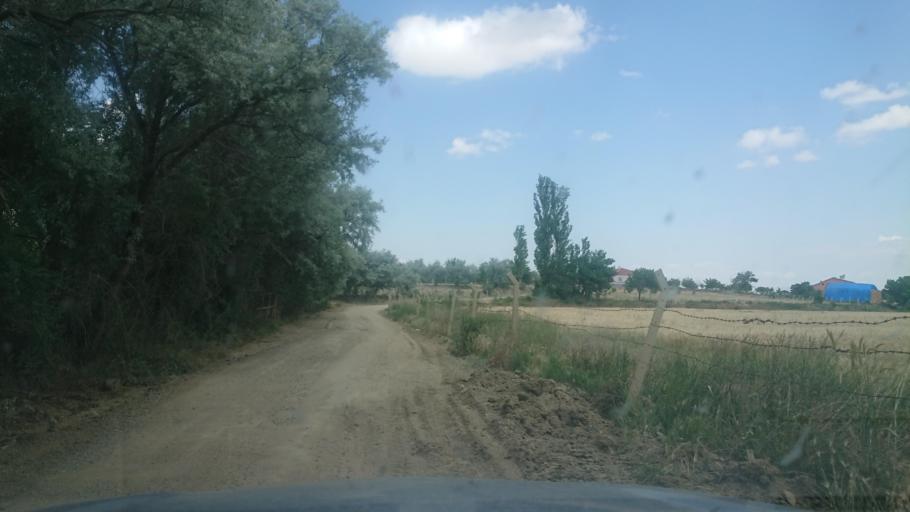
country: TR
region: Aksaray
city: Agacoren
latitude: 38.9331
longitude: 33.9536
